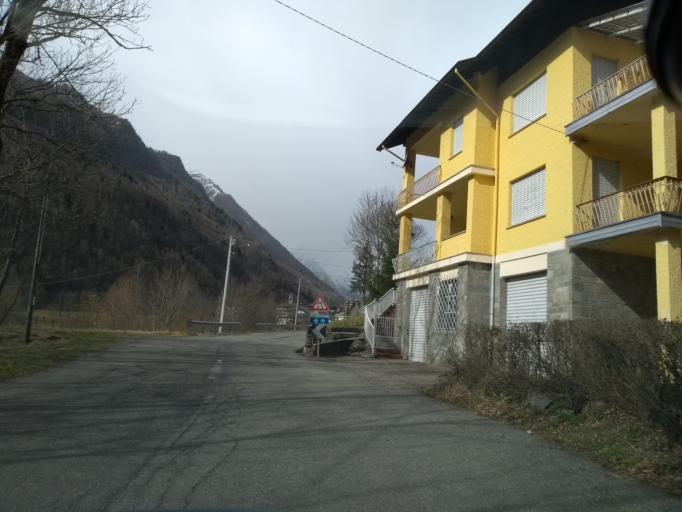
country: IT
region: Piedmont
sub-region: Provincia di Torino
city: Chialamberto
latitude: 45.3672
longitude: 7.3278
